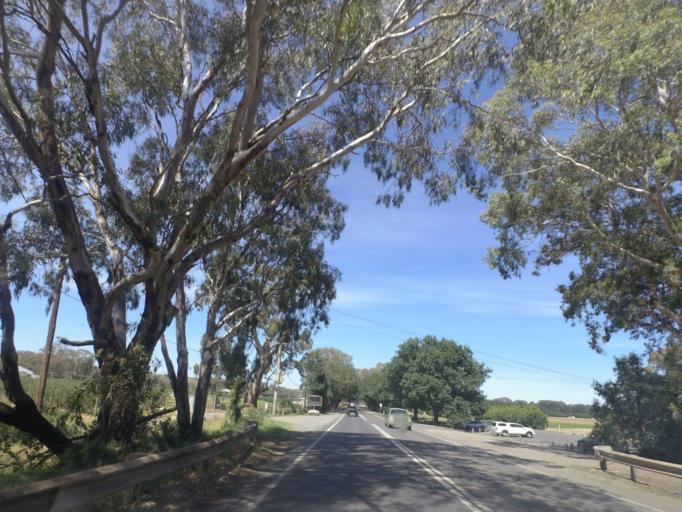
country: AU
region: Victoria
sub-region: Moorabool
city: Bacchus Marsh
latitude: -37.6867
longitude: 144.4788
